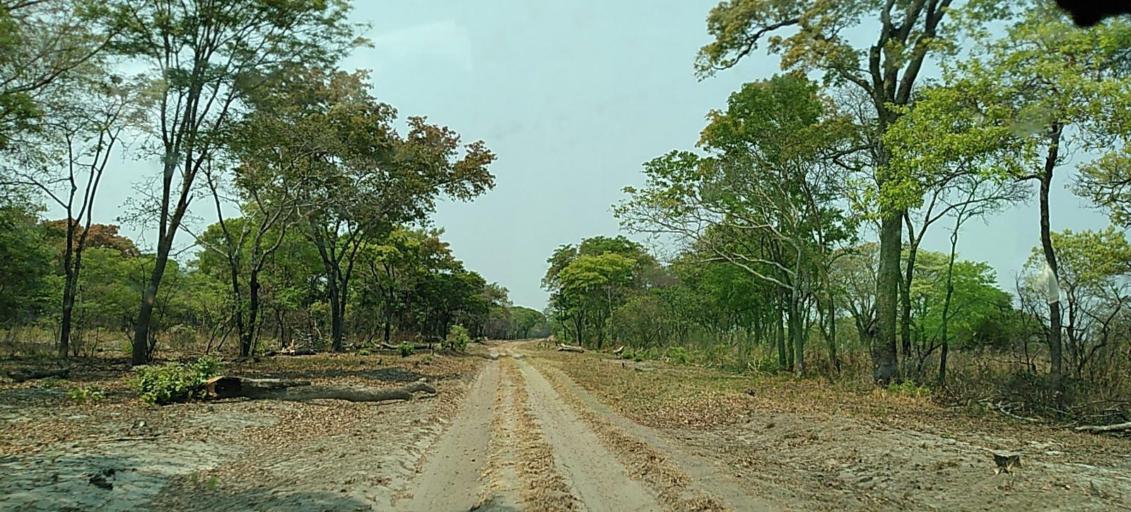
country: ZM
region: Western
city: Lukulu
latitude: -13.9505
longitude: 23.2240
